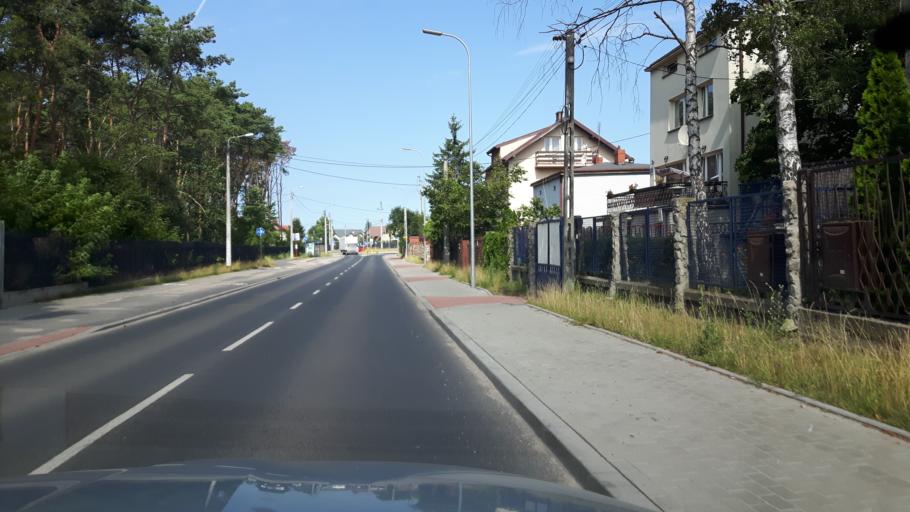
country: PL
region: Masovian Voivodeship
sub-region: Powiat wolominski
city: Marki
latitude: 52.3196
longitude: 21.0965
